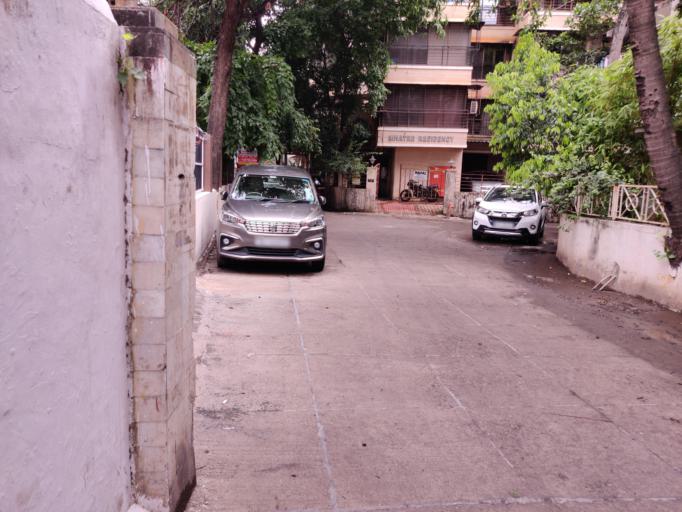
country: IN
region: Maharashtra
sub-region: Mumbai Suburban
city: Borivli
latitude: 19.2557
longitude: 72.8569
